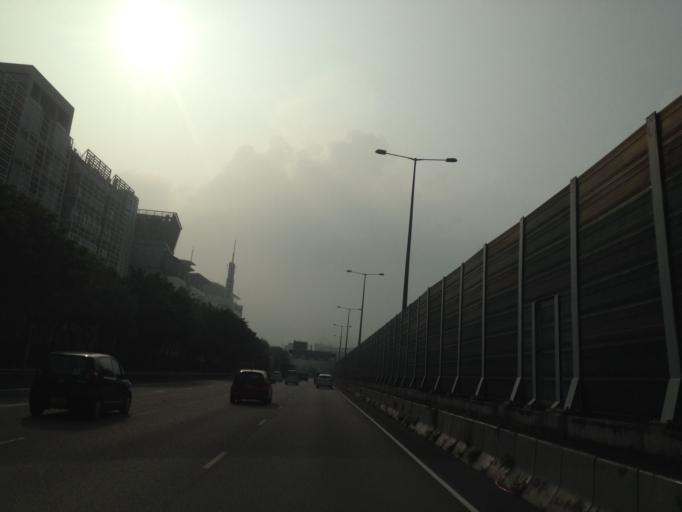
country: HK
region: Tai Po
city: Tai Po
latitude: 22.4258
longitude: 114.2088
